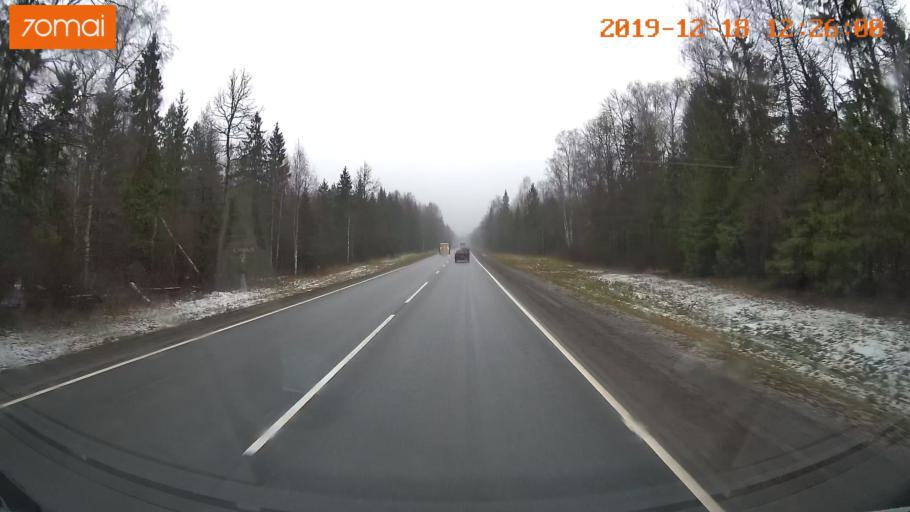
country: RU
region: Moskovskaya
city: Novopetrovskoye
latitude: 56.0458
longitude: 36.4996
